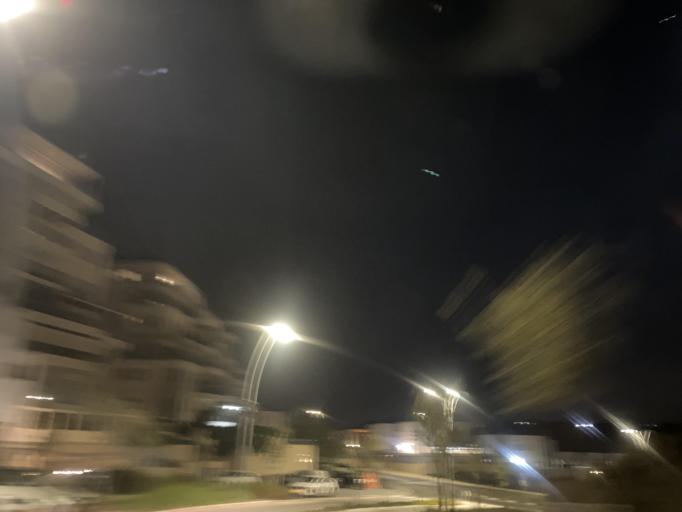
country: IL
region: Haifa
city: Daliyat el Karmil
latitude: 32.6358
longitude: 35.0773
